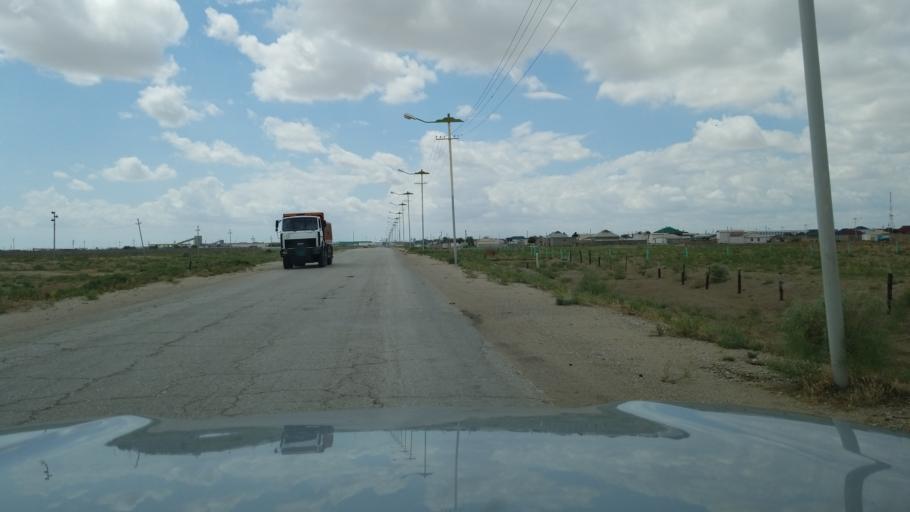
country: TM
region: Balkan
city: Balkanabat
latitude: 39.4904
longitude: 54.3952
